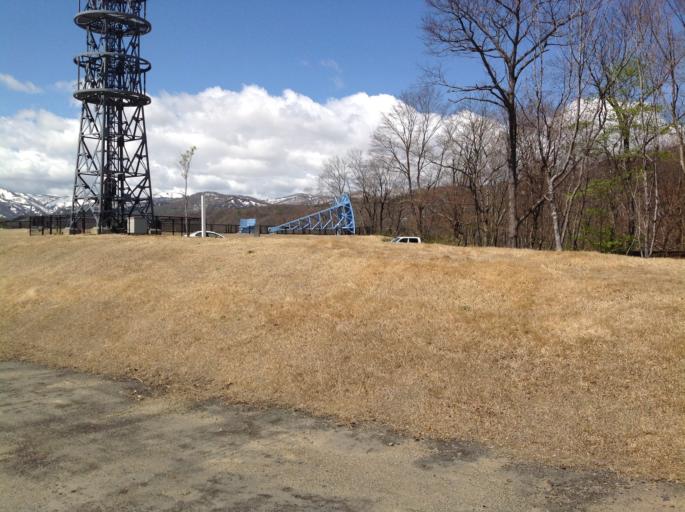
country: JP
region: Iwate
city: Mizusawa
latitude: 39.1160
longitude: 140.9034
